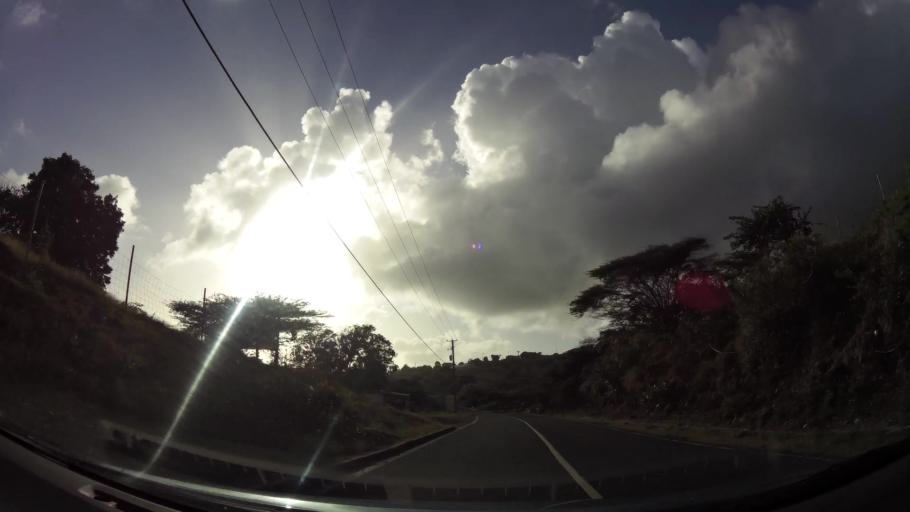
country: KN
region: Saint George Gingerland
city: Market Shop
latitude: 17.1316
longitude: -62.5763
